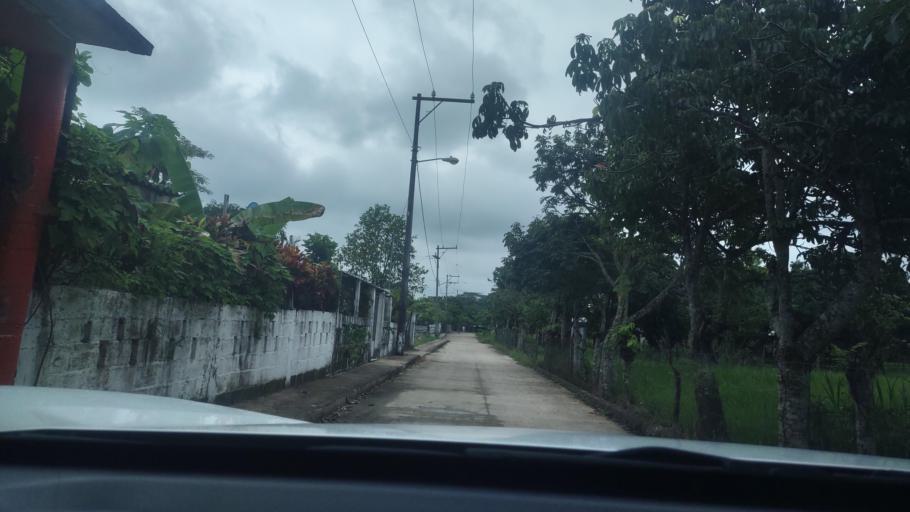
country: MX
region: Veracruz
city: Villa Nanchital
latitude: 18.0416
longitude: -94.3515
